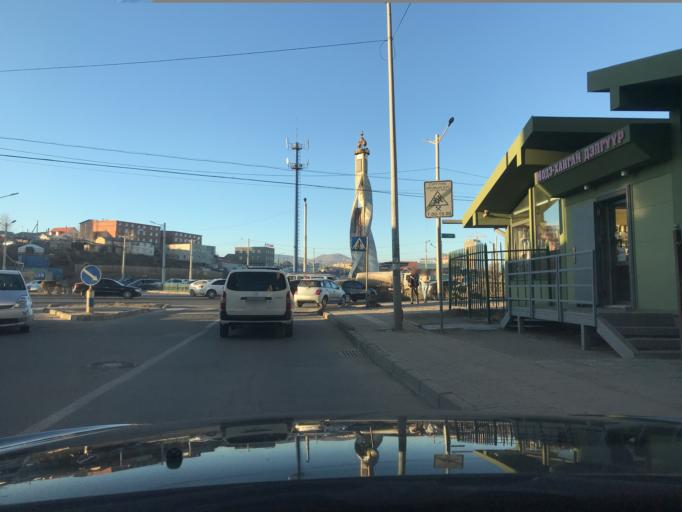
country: MN
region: Ulaanbaatar
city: Ulaanbaatar
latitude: 47.9275
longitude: 106.9053
